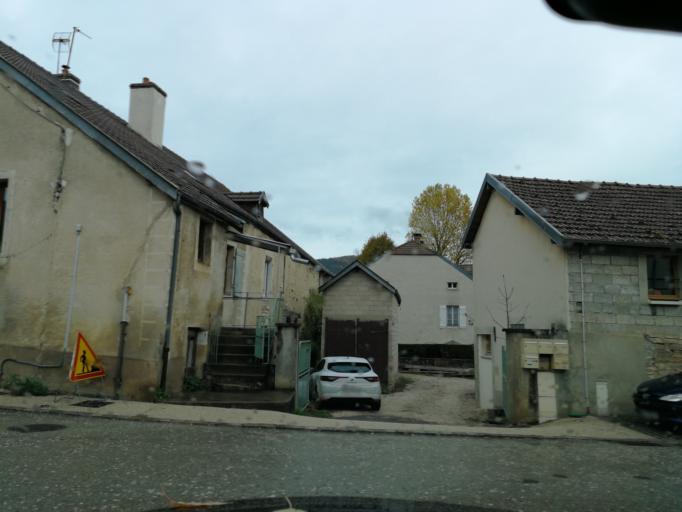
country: FR
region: Bourgogne
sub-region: Departement de la Cote-d'Or
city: Fleurey-sur-Ouche
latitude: 47.3229
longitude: 4.7924
